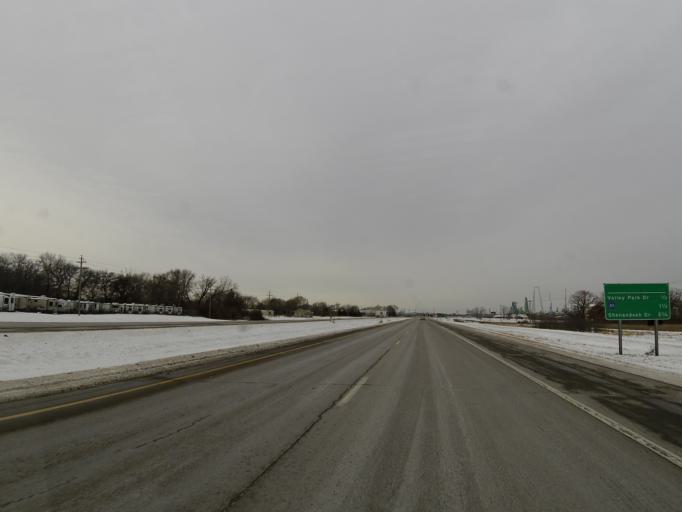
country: US
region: Minnesota
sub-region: Hennepin County
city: Eden Prairie
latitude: 44.7956
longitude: -93.4396
